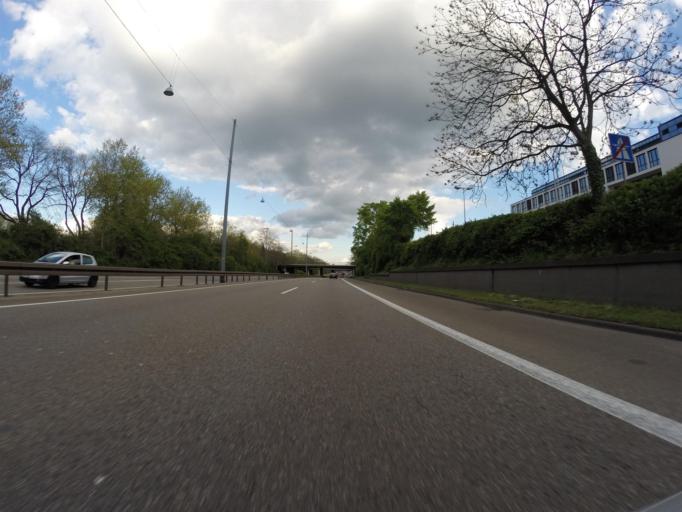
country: DE
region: Saarland
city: Saarbrucken
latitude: 49.2283
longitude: 6.9988
